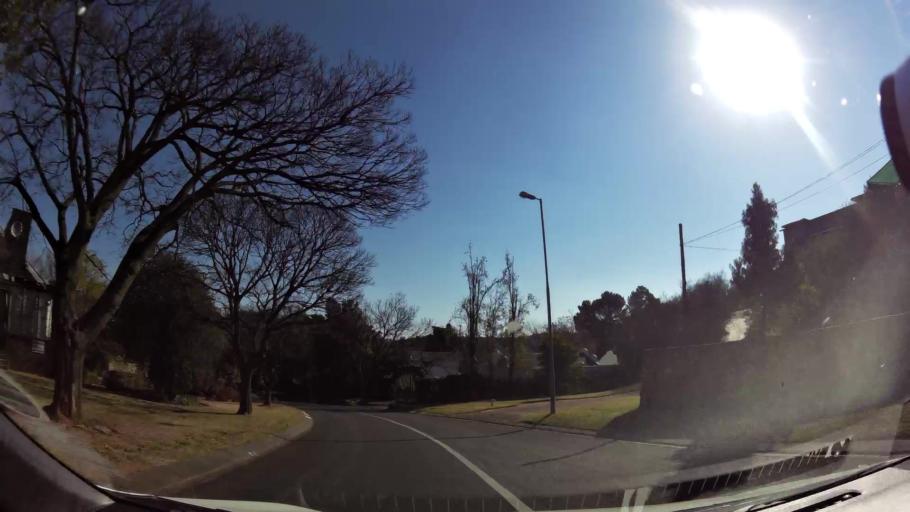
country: ZA
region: Gauteng
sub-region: City of Johannesburg Metropolitan Municipality
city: Johannesburg
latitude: -26.2708
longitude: 28.0133
